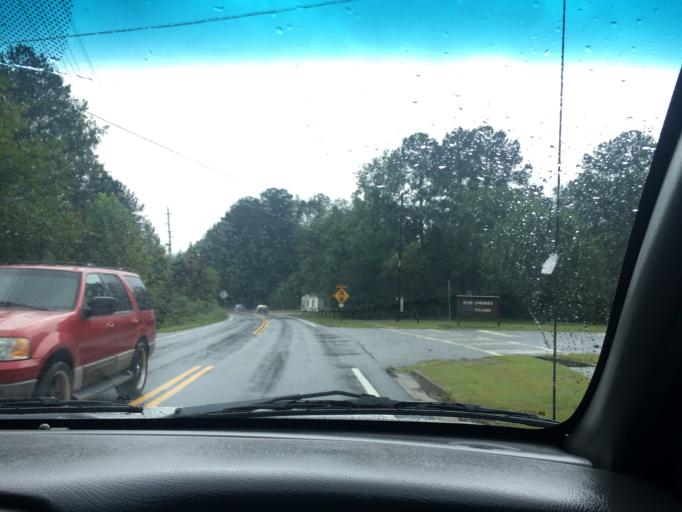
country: US
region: Georgia
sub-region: Cobb County
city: Acworth
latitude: 34.0410
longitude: -84.6533
